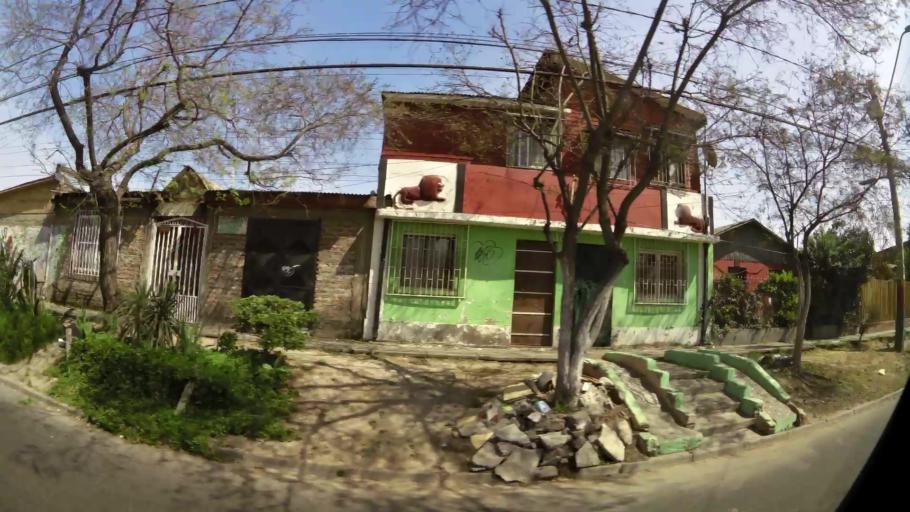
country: CL
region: Santiago Metropolitan
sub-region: Provincia de Santiago
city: Lo Prado
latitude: -33.4314
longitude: -70.7304
